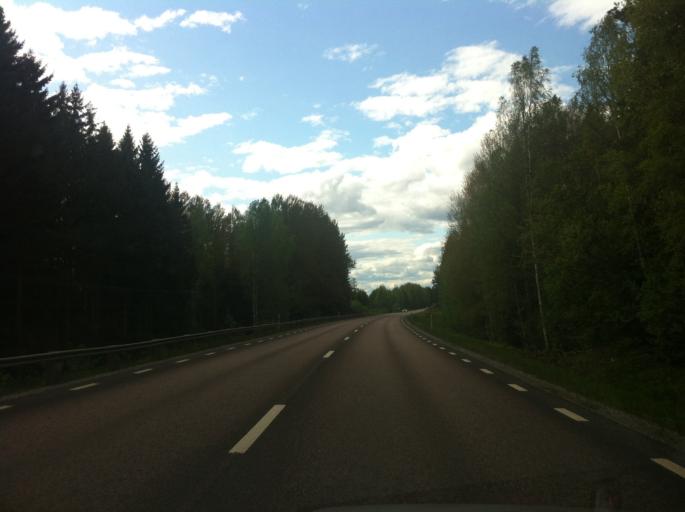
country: SE
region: Vaermland
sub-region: Filipstads Kommun
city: Filipstad
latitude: 59.6576
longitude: 14.2225
